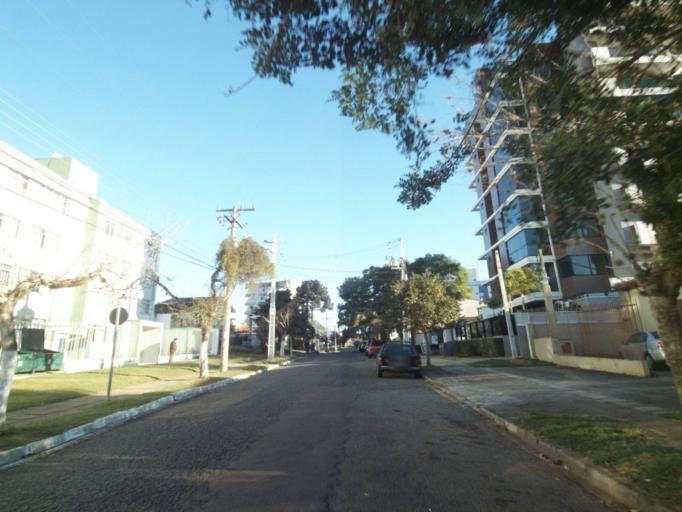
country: BR
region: Parana
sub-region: Curitiba
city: Curitiba
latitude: -25.4602
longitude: -49.2952
